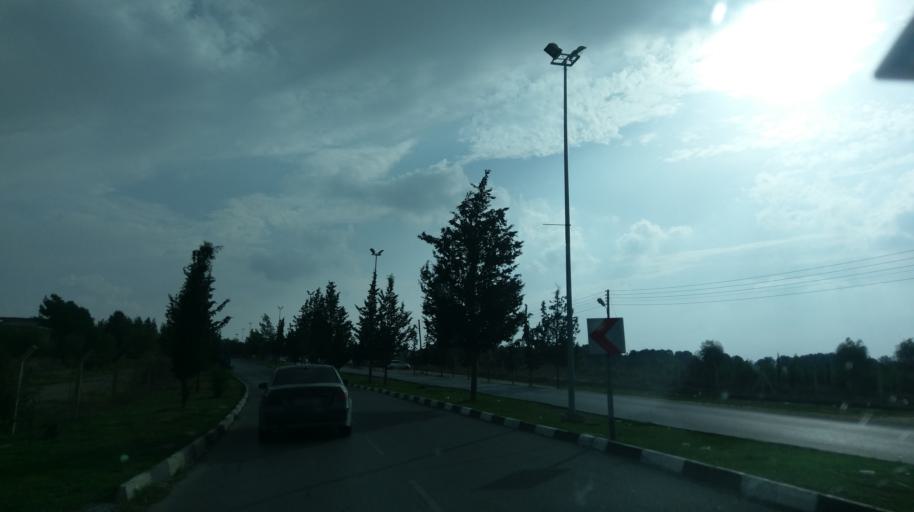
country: CY
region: Lefkosia
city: Nicosia
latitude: 35.1847
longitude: 33.3229
